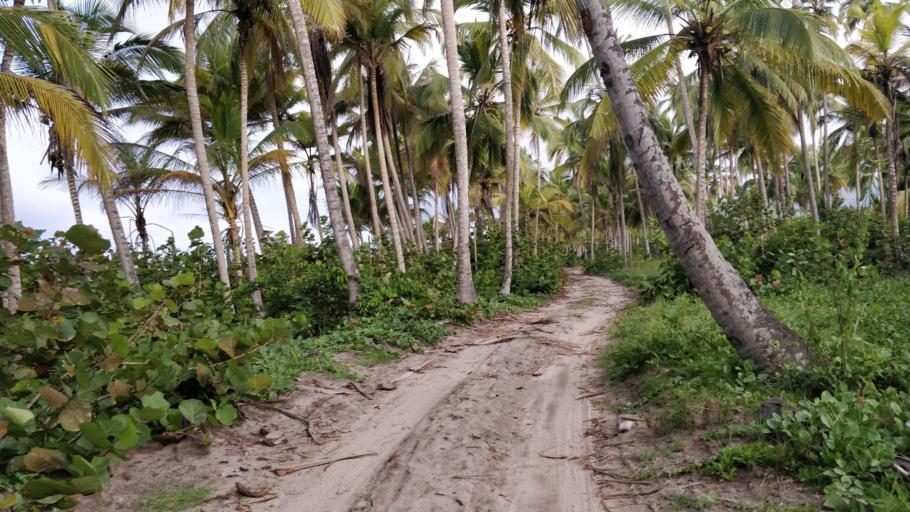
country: CO
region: Magdalena
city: Santa Marta
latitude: 11.2709
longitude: -73.8421
